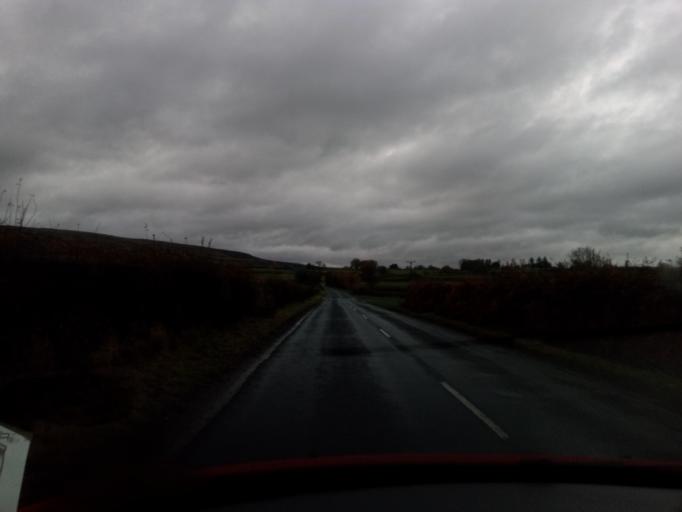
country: GB
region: England
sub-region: County Durham
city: Muggleswick
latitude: 54.8516
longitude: -1.9615
